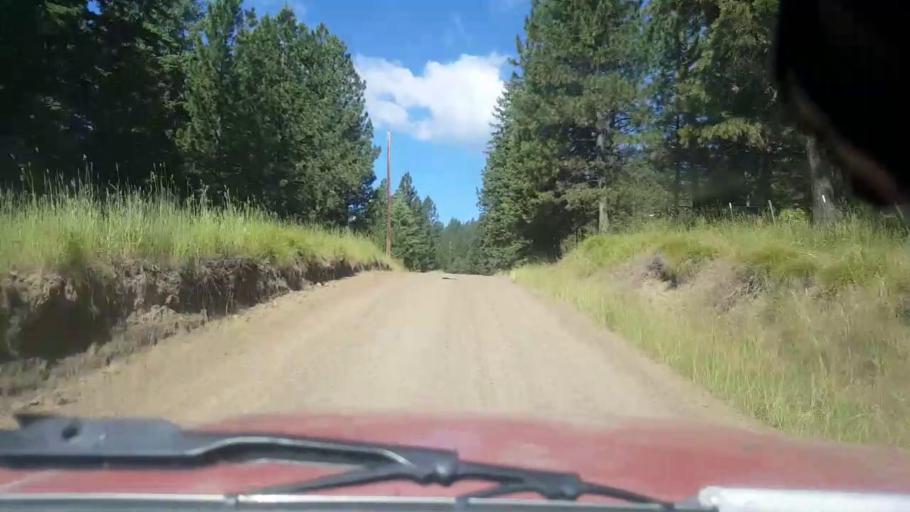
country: US
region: Washington
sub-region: Garfield County
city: Pomeroy
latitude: 46.0370
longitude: -117.4416
